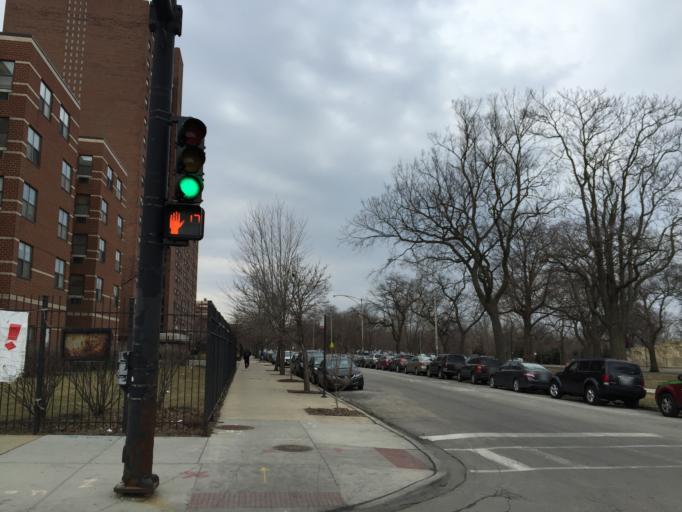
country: US
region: Illinois
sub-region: Cook County
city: Chicago
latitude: 41.7858
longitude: -87.6061
